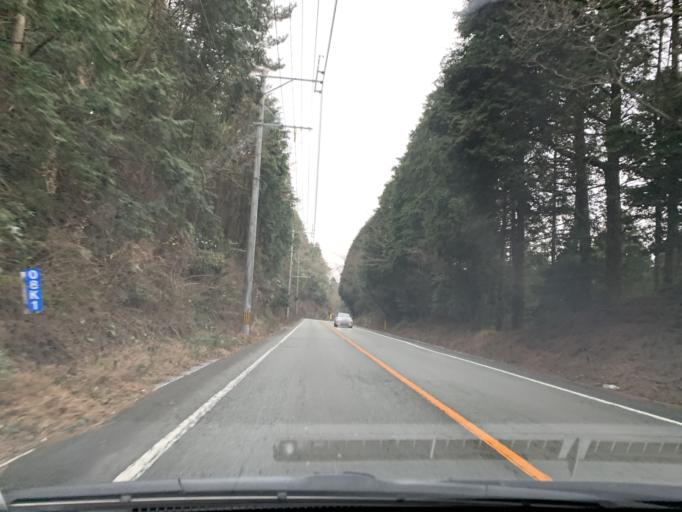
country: JP
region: Kumamoto
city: Ozu
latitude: 32.9022
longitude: 130.9417
